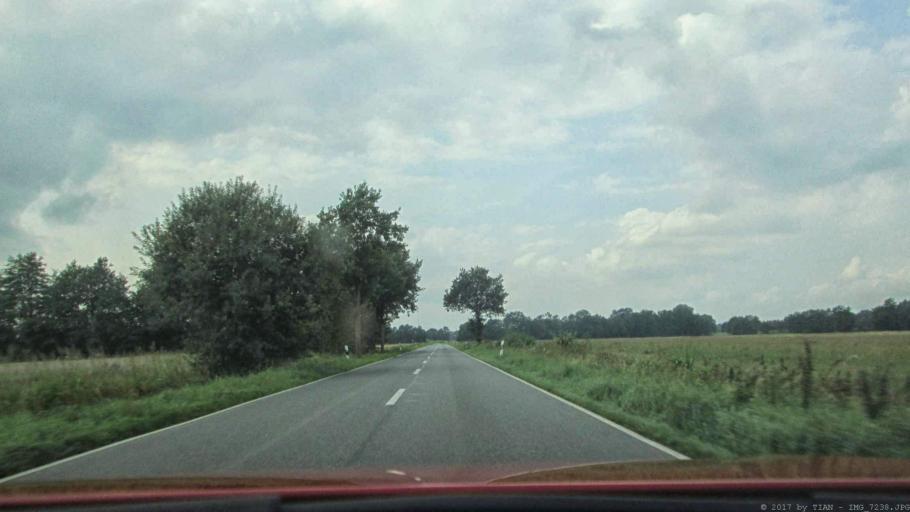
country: DE
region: Lower Saxony
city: Hittbergen
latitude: 53.3164
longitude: 10.6219
